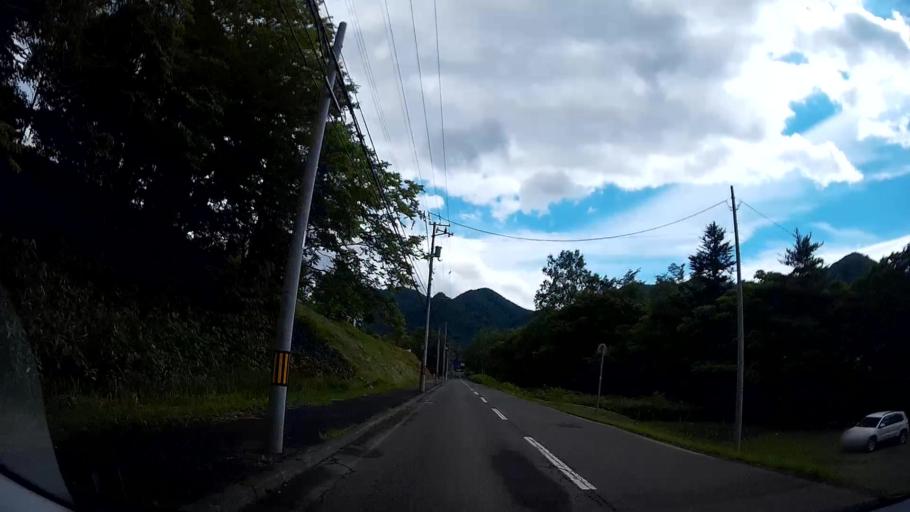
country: JP
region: Hokkaido
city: Sapporo
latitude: 42.9460
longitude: 141.1546
